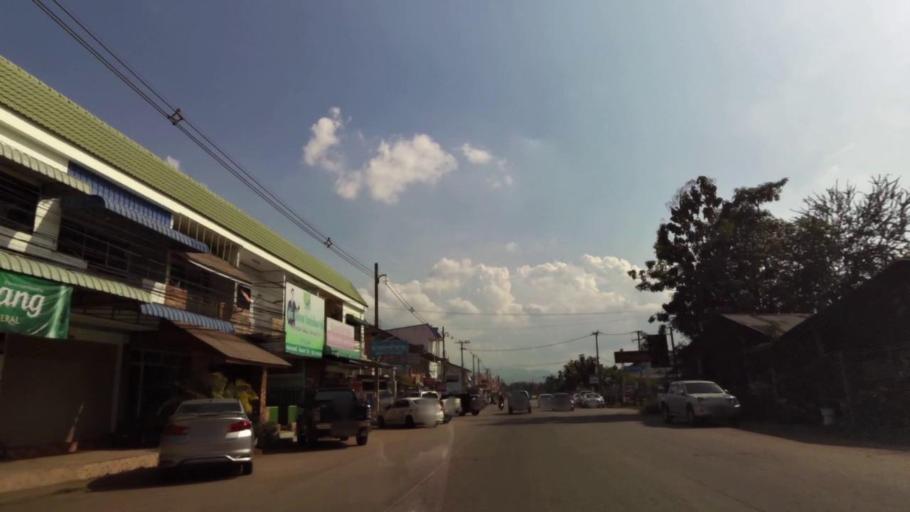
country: TH
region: Phrae
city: Phrae
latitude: 18.1224
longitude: 100.1533
